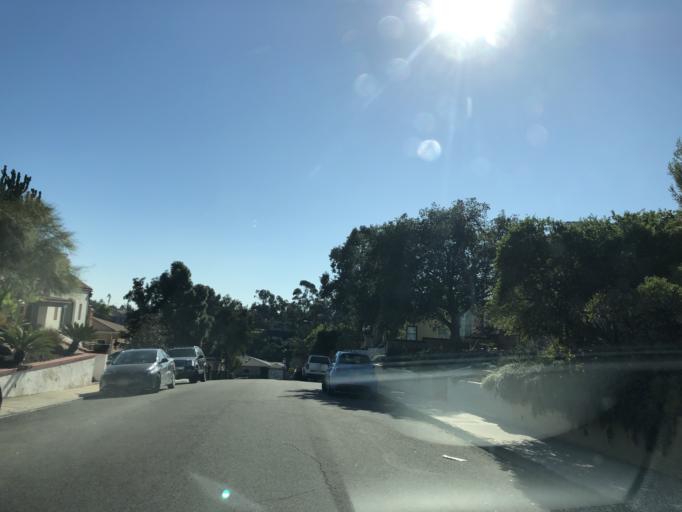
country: US
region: California
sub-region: San Diego County
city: San Diego
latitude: 32.7347
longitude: -117.1304
